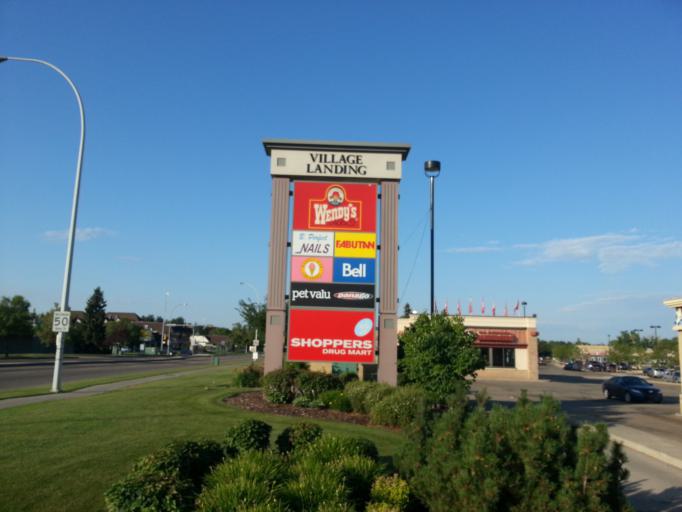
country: CA
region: Alberta
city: St. Albert
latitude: 53.6213
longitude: -113.6102
